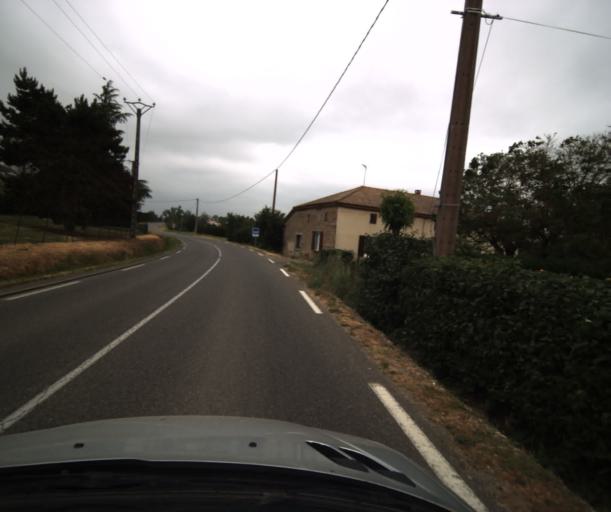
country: FR
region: Midi-Pyrenees
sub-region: Departement du Tarn-et-Garonne
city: Saint-Nicolas-de-la-Grave
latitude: 44.0369
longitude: 1.0379
